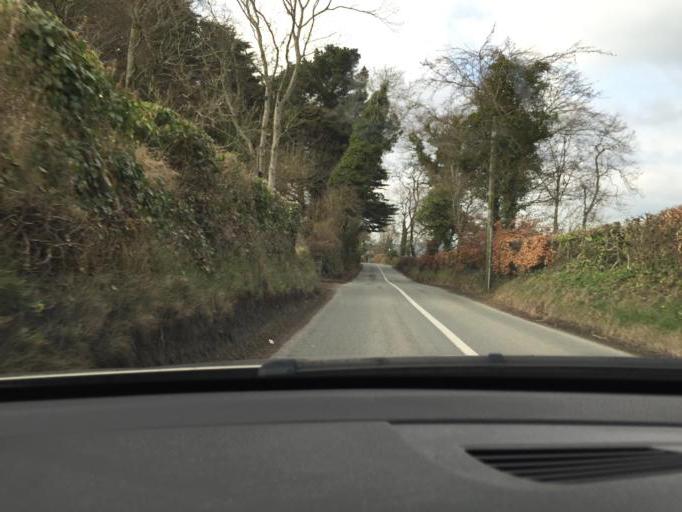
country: IE
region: Leinster
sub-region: Wicklow
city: Blessington
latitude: 53.1375
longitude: -6.5240
